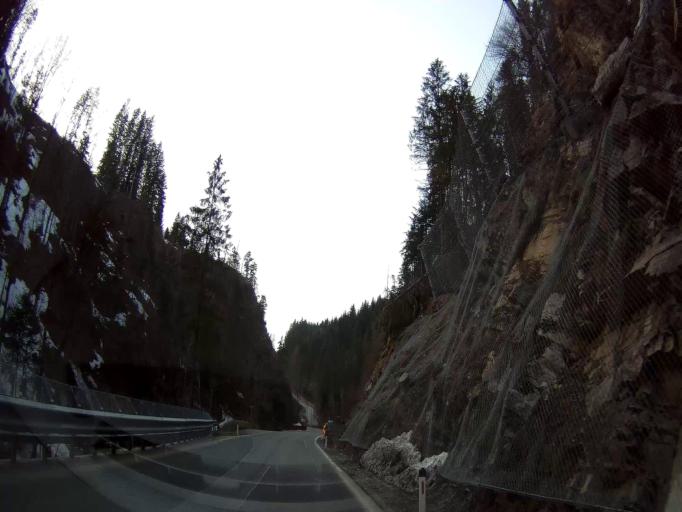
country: AT
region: Salzburg
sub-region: Politischer Bezirk Hallein
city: Abtenau
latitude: 47.5442
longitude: 13.4205
